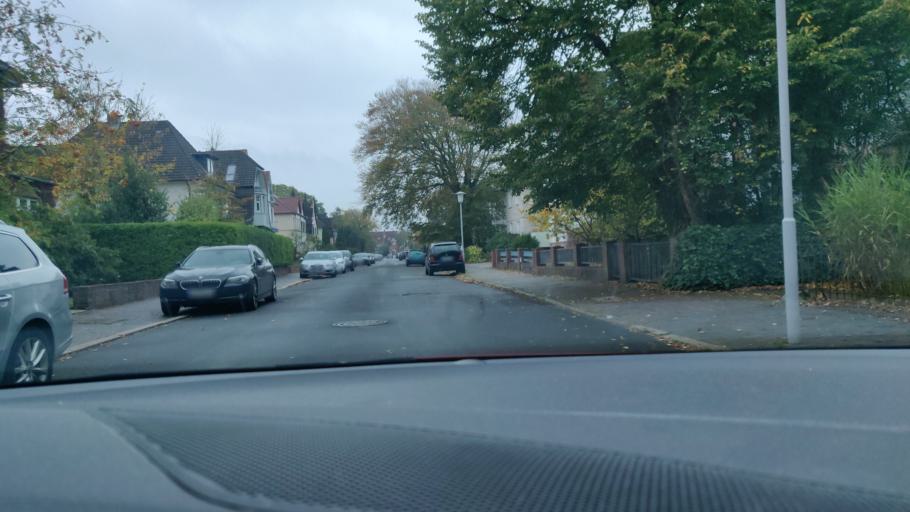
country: DE
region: Lower Saxony
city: Cuxhaven
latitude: 53.8731
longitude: 8.6928
